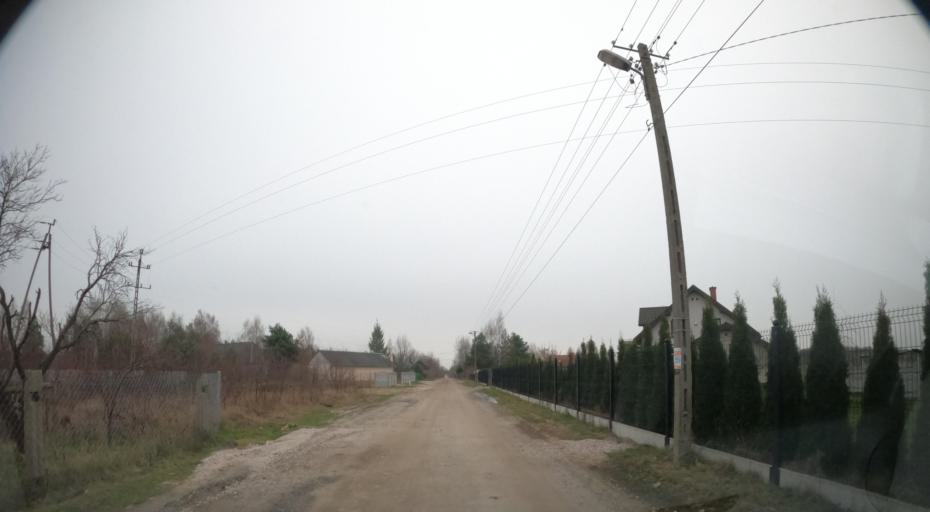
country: PL
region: Masovian Voivodeship
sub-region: Powiat radomski
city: Jastrzebia
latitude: 51.4878
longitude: 21.1883
